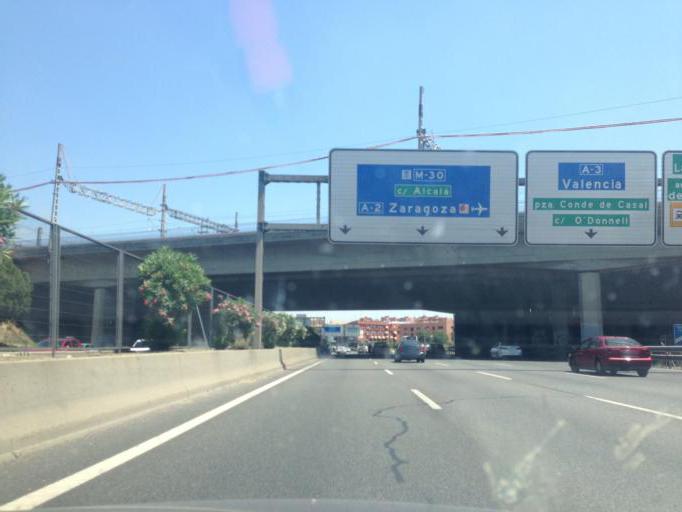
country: ES
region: Madrid
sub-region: Provincia de Madrid
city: Puente de Vallecas
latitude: 40.3938
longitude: -3.6745
